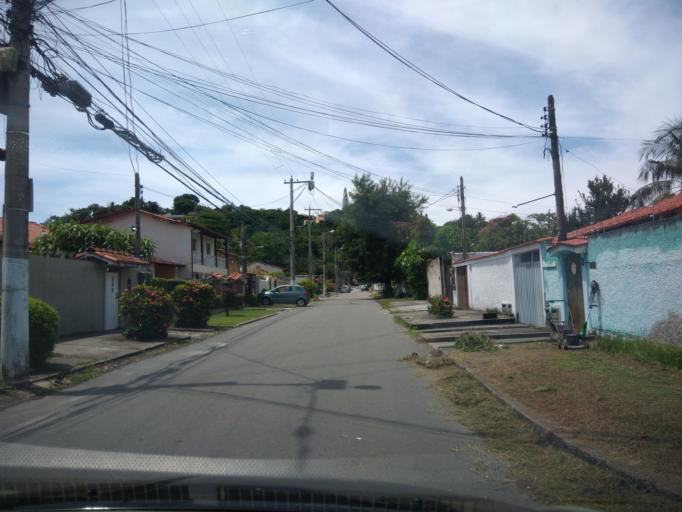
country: BR
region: Rio de Janeiro
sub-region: Niteroi
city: Niteroi
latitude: -22.9394
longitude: -43.0633
